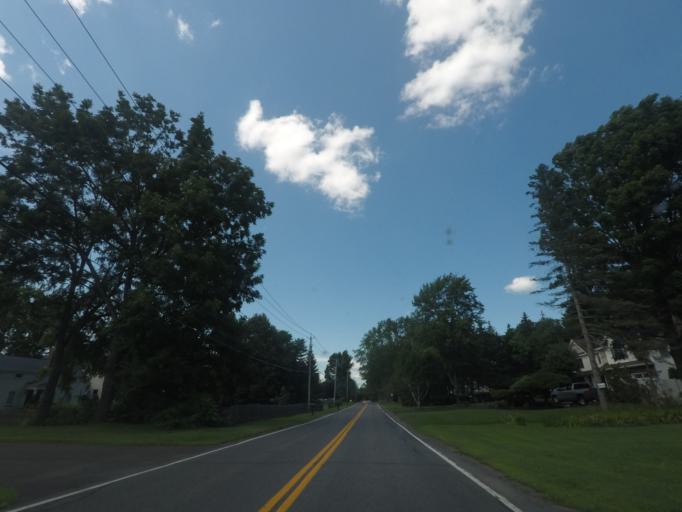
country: US
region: New York
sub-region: Schenectady County
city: Rotterdam
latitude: 42.7615
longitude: -73.9615
